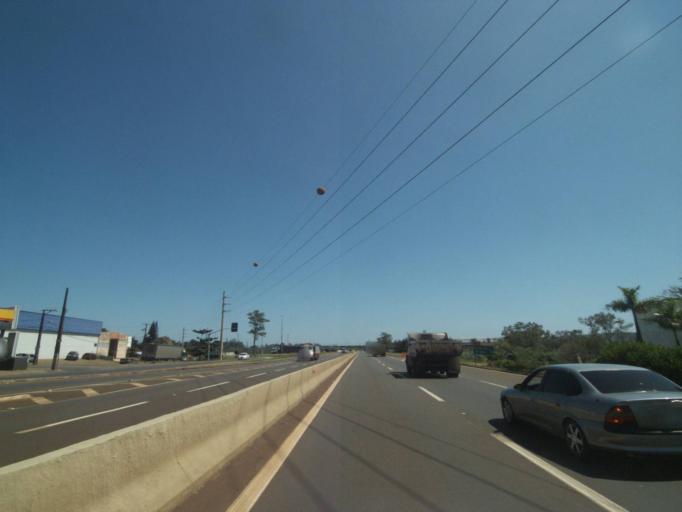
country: BR
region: Parana
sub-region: Cambe
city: Cambe
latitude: -23.2884
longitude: -51.2350
